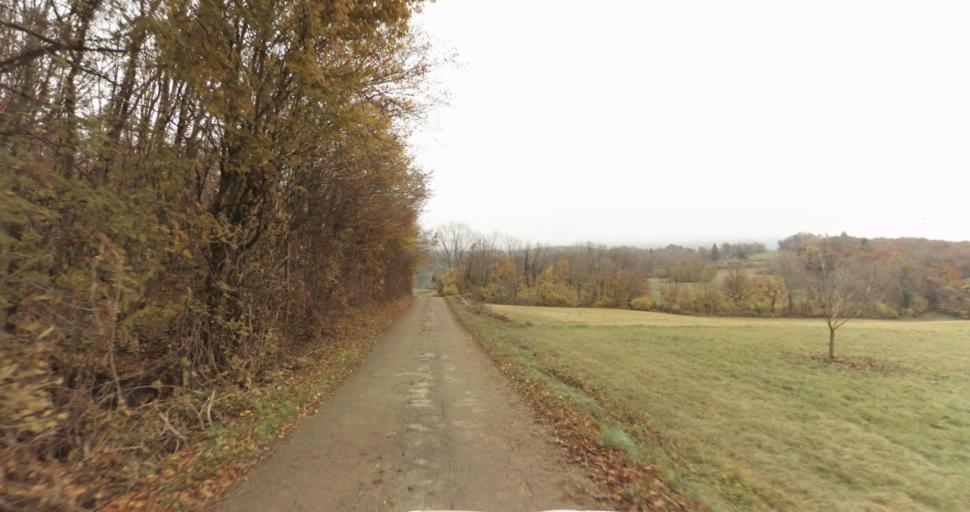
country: FR
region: Rhone-Alpes
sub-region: Departement de la Haute-Savoie
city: Cusy
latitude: 45.7543
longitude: 6.0112
